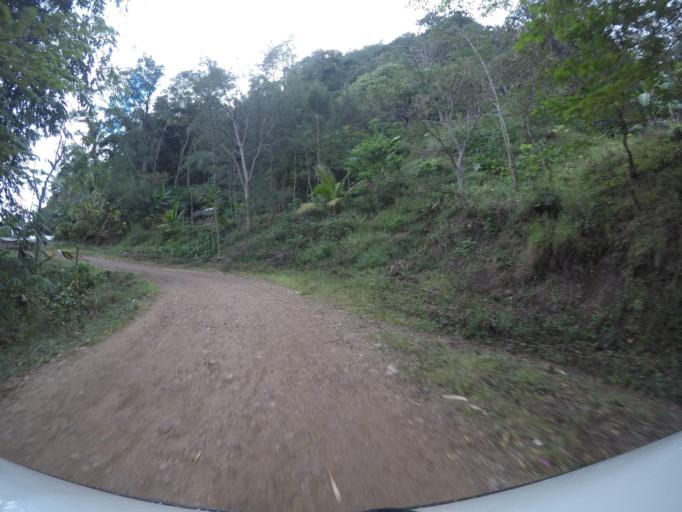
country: TL
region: Baucau
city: Baucau
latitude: -8.6464
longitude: 126.6266
